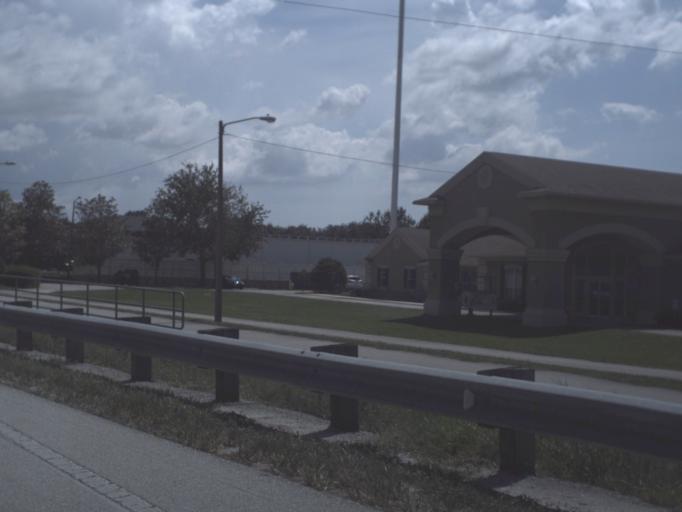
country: US
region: Florida
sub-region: Pinellas County
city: East Lake
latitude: 28.1276
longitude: -82.6972
